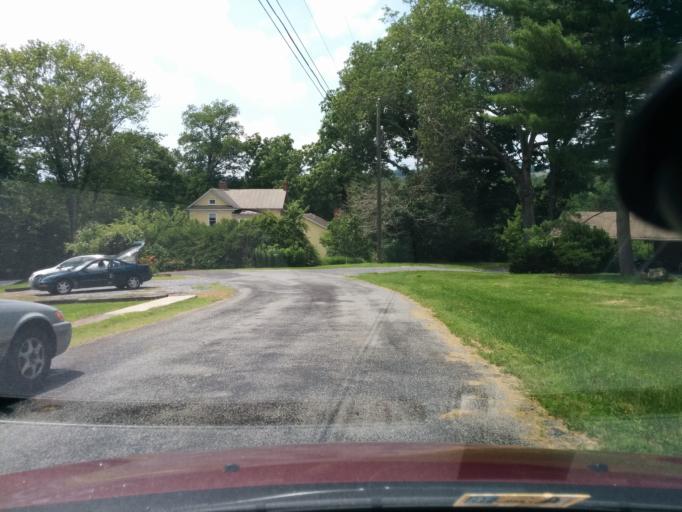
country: US
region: Virginia
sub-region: Rockbridge County
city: East Lexington
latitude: 37.8183
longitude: -79.3989
